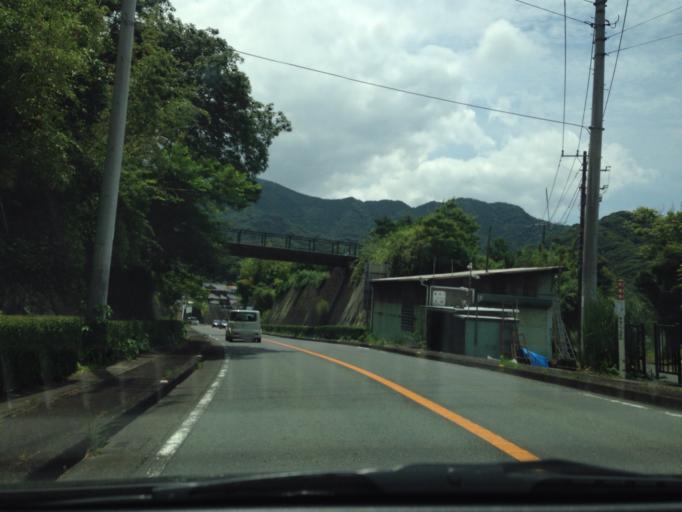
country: JP
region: Shizuoka
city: Heda
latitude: 34.8137
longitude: 138.7717
